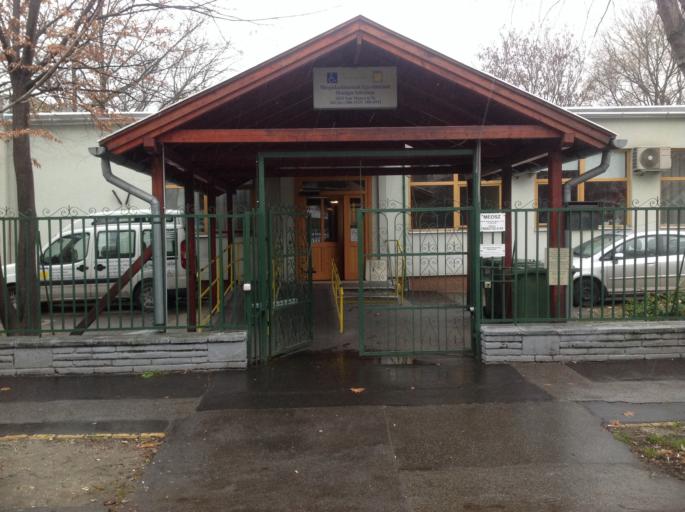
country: HU
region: Budapest
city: Budapest III. keruelet
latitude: 47.5409
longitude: 19.0337
